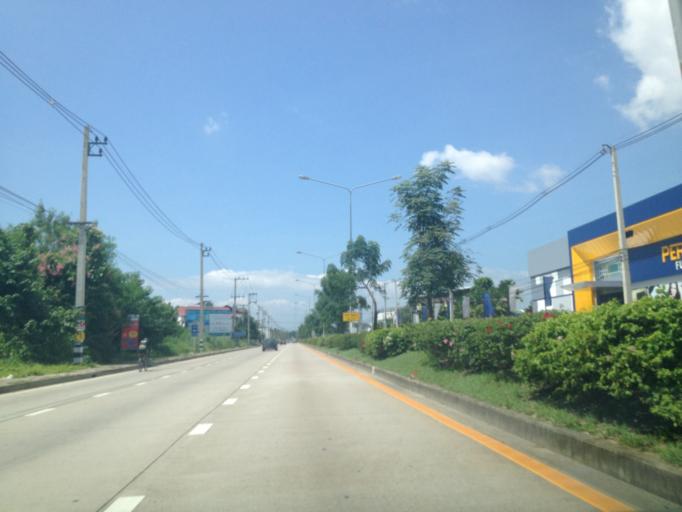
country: TH
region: Chiang Mai
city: Chiang Mai
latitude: 18.7450
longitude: 98.9789
